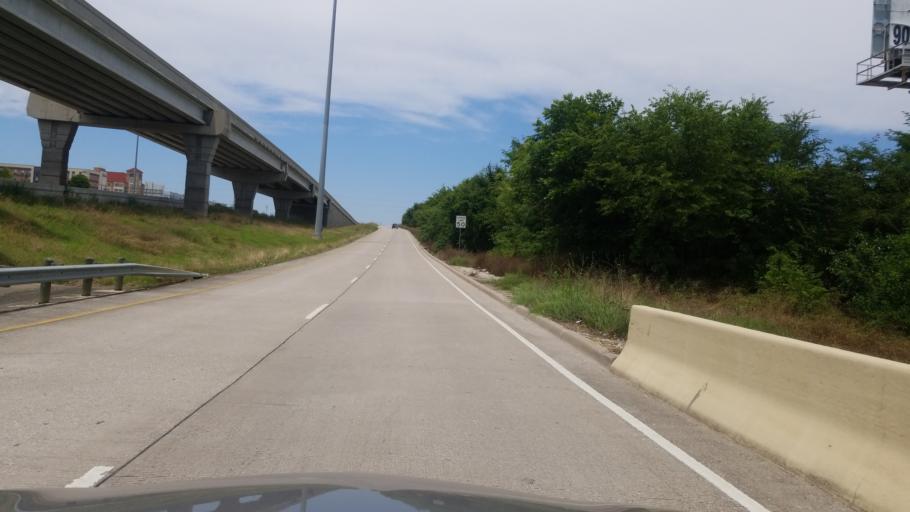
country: US
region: Texas
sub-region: Dallas County
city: Grand Prairie
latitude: 32.6766
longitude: -97.0272
